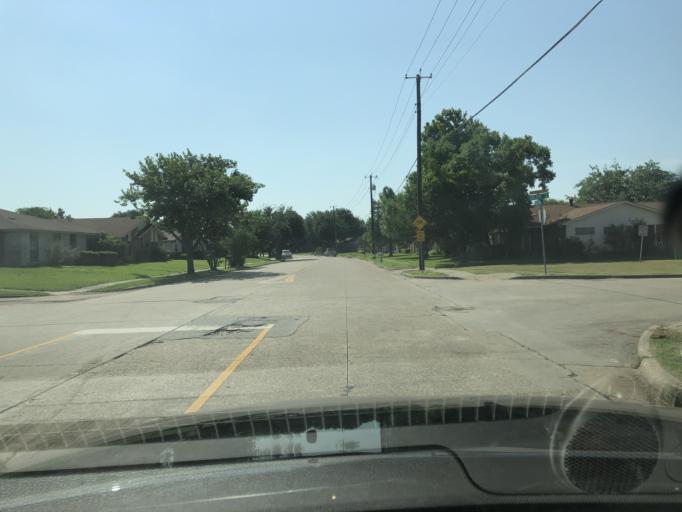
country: US
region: Texas
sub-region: Dallas County
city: Sunnyvale
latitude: 32.8385
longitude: -96.5766
